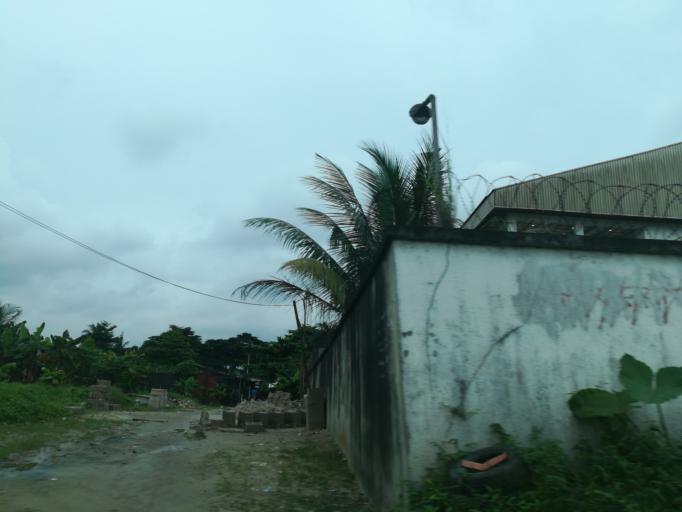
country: NG
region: Rivers
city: Port Harcourt
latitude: 4.8174
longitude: 6.9941
